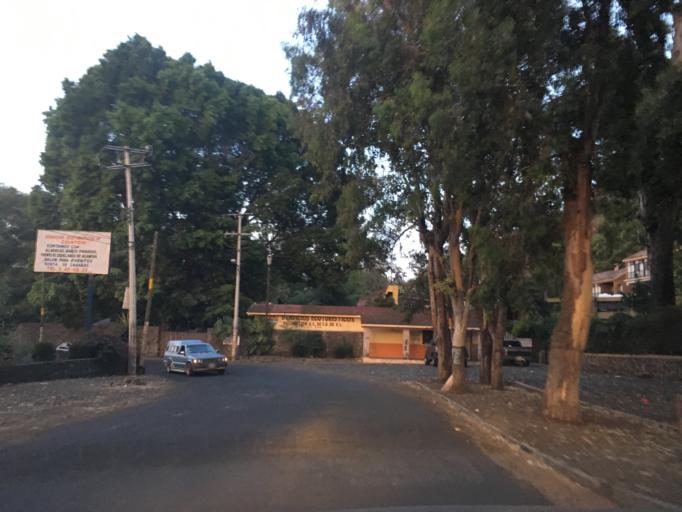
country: MX
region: Michoacan
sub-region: Morelia
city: La Mintzita (Piedra Dura)
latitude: 19.6398
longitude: -101.2753
